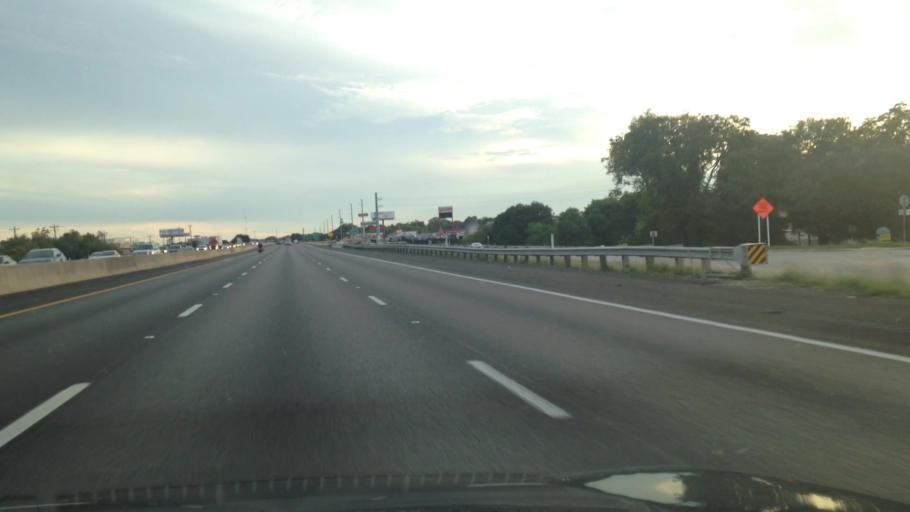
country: US
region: Texas
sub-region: Hays County
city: Kyle
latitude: 30.0044
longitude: -97.8661
